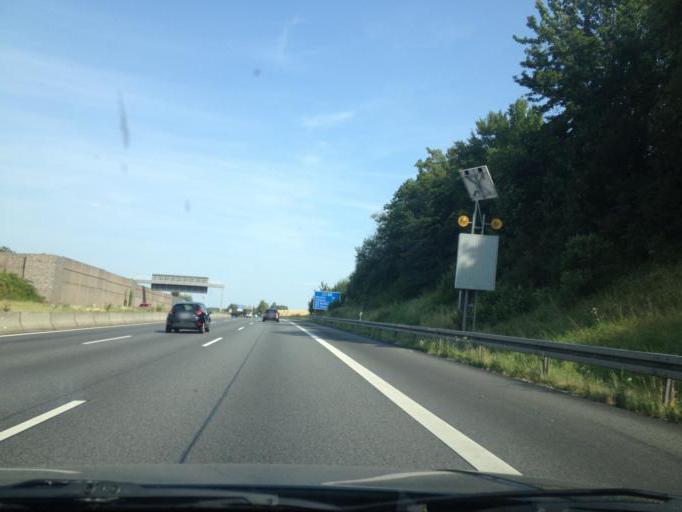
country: DE
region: Baden-Wuerttemberg
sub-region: Karlsruhe Region
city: Sinsheim
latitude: 49.2467
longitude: 8.8621
